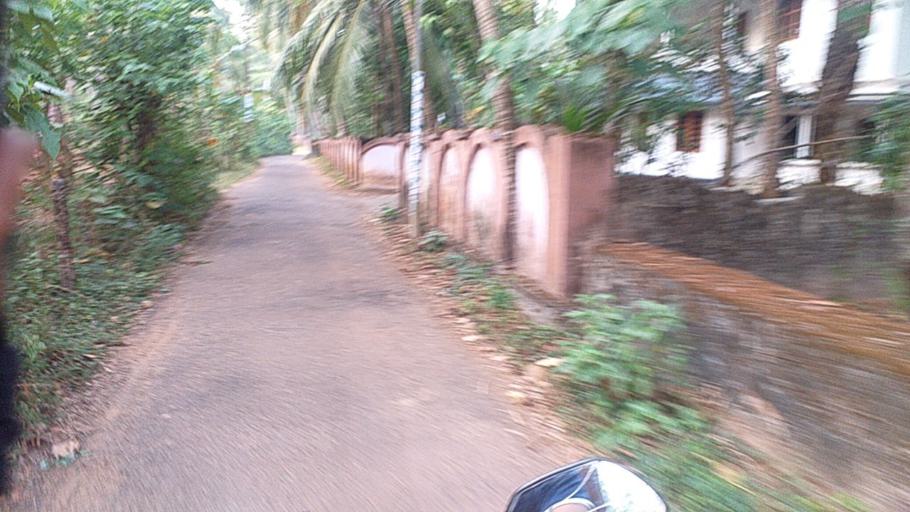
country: IN
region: Kerala
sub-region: Thrissur District
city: Kunnamkulam
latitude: 10.7379
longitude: 76.0411
